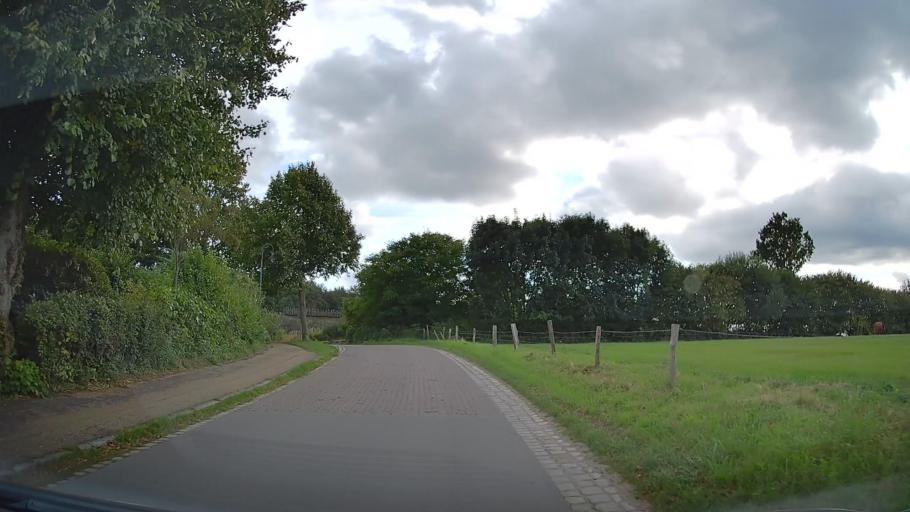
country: DE
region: Schleswig-Holstein
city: Steinberg
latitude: 54.7763
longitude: 9.7999
